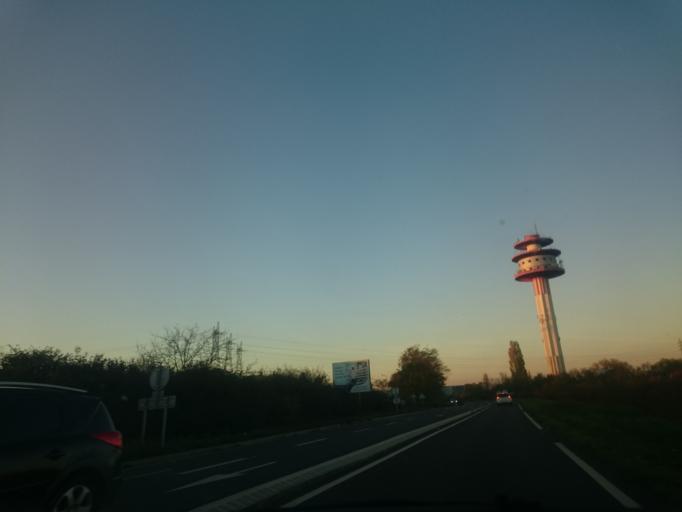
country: FR
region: Ile-de-France
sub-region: Departement de l'Essonne
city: Villabe
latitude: 48.5976
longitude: 2.4427
